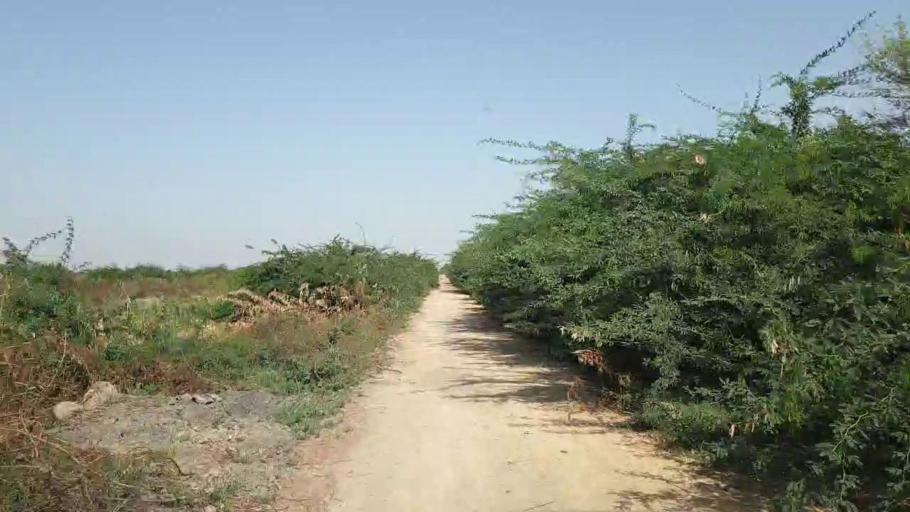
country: PK
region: Sindh
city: Tando Bago
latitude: 24.7201
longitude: 69.0730
